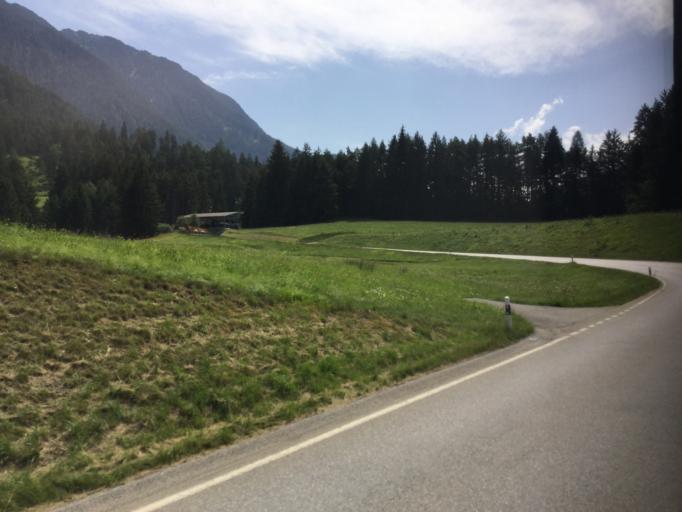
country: CH
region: Grisons
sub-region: Albula District
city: Tiefencastel
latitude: 46.6553
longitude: 9.5747
